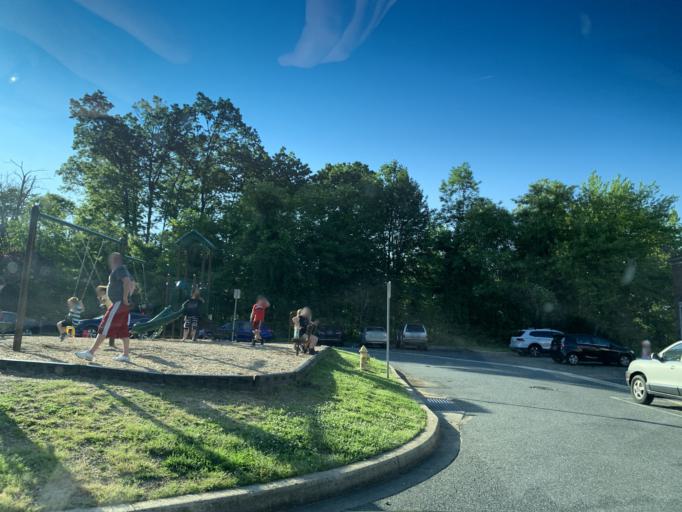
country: US
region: Maryland
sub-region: Harford County
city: Riverside
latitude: 39.4697
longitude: -76.2680
